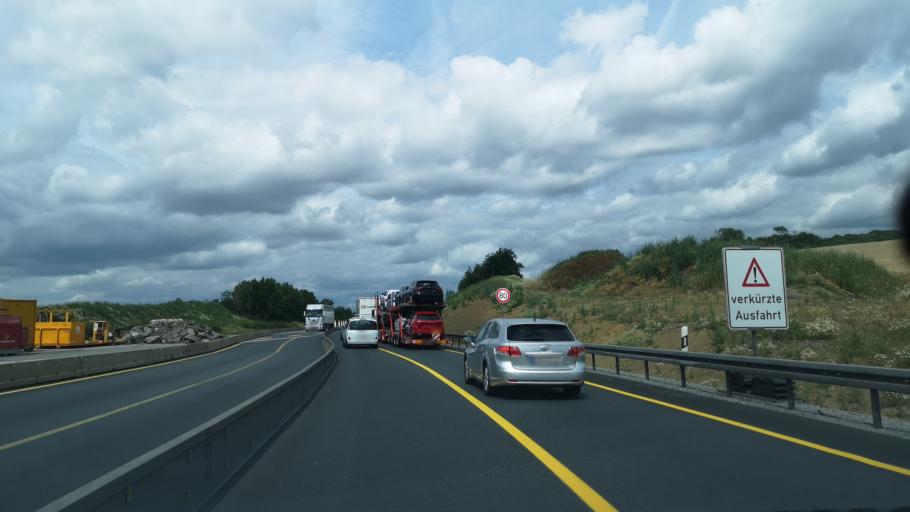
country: DE
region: Bavaria
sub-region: Regierungsbezirk Unterfranken
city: Kurnach
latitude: 49.8438
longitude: 10.0202
